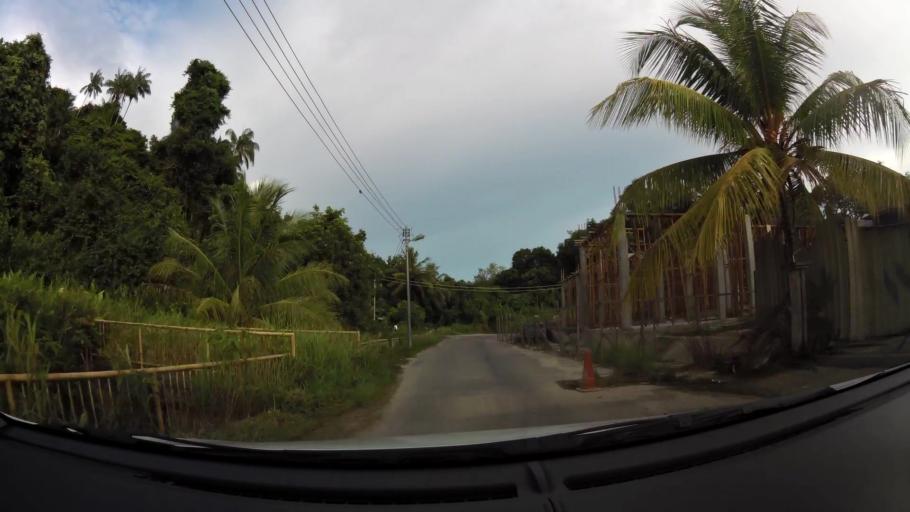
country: BN
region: Brunei and Muara
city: Bandar Seri Begawan
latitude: 4.9741
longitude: 114.9869
